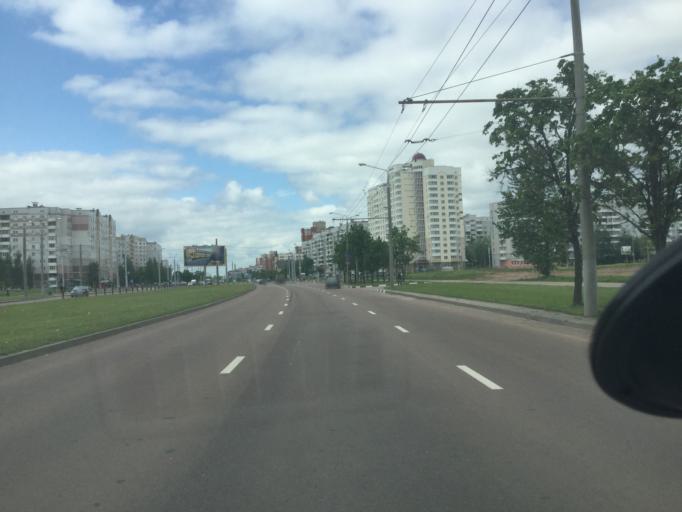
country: BY
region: Vitebsk
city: Vitebsk
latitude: 55.1612
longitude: 30.2247
